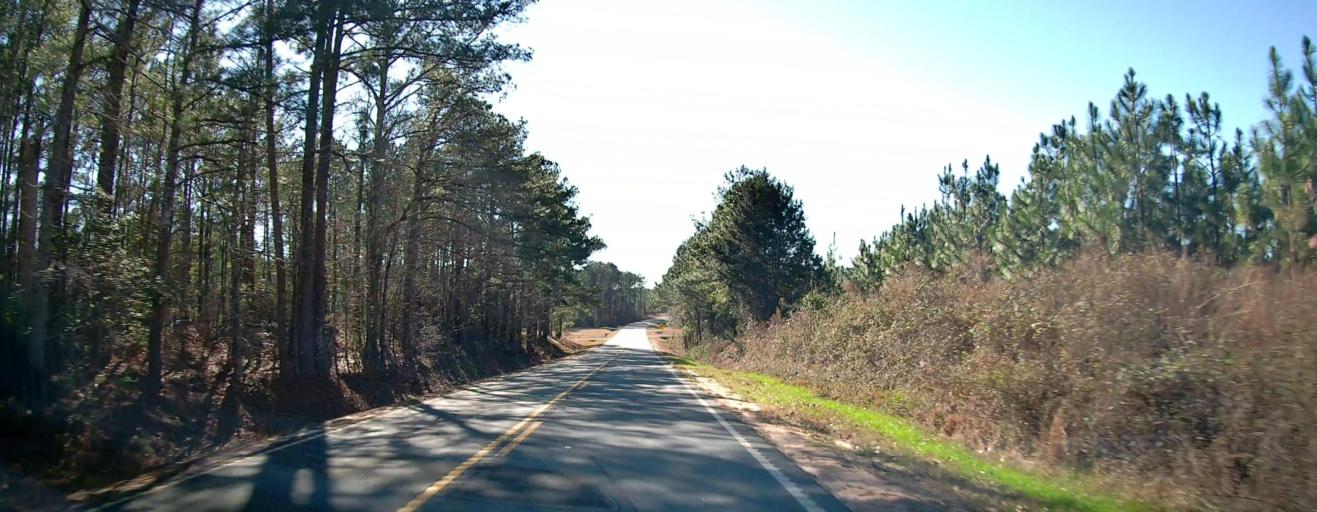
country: US
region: Georgia
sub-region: Taylor County
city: Butler
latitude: 32.6607
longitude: -84.3452
